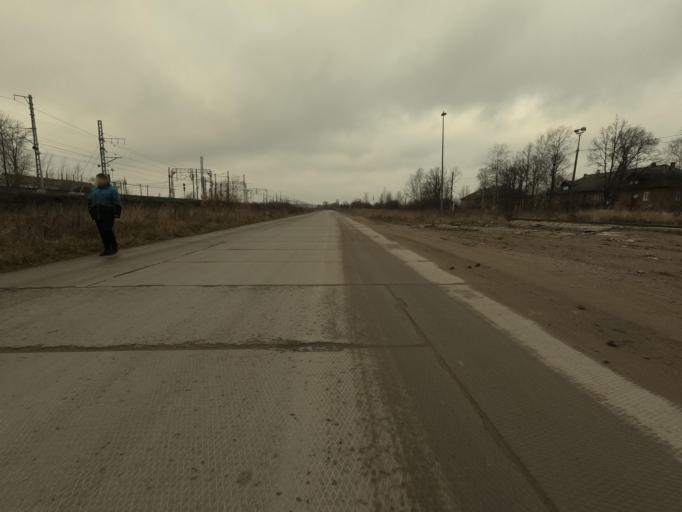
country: RU
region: Leningrad
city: Lyuban'
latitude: 59.4751
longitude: 31.2561
